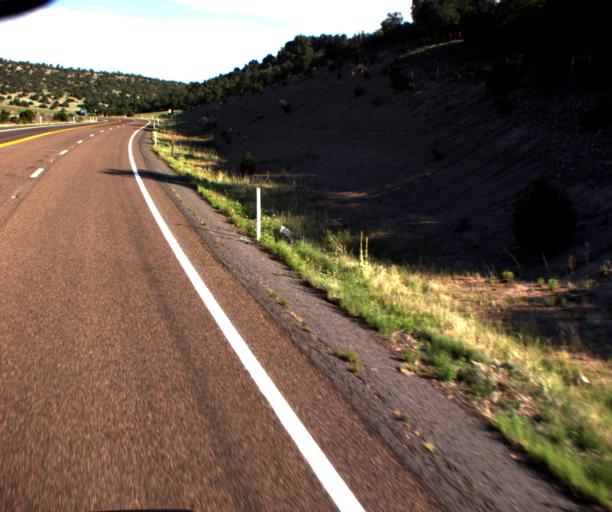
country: US
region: Arizona
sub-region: Apache County
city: Eagar
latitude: 34.0961
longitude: -109.2133
